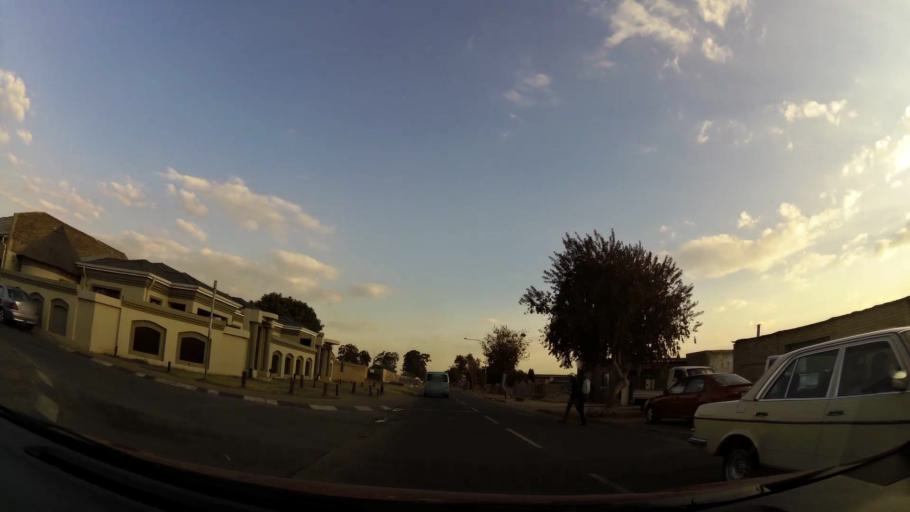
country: ZA
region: Gauteng
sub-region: City of Johannesburg Metropolitan Municipality
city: Roodepoort
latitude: -26.2135
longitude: 27.8944
